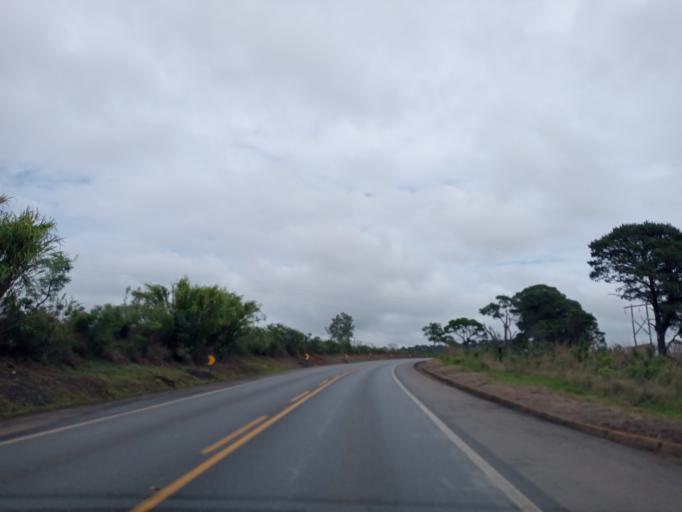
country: BR
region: Minas Gerais
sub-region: Campos Altos
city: Campos Altos
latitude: -19.6601
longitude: -46.2024
